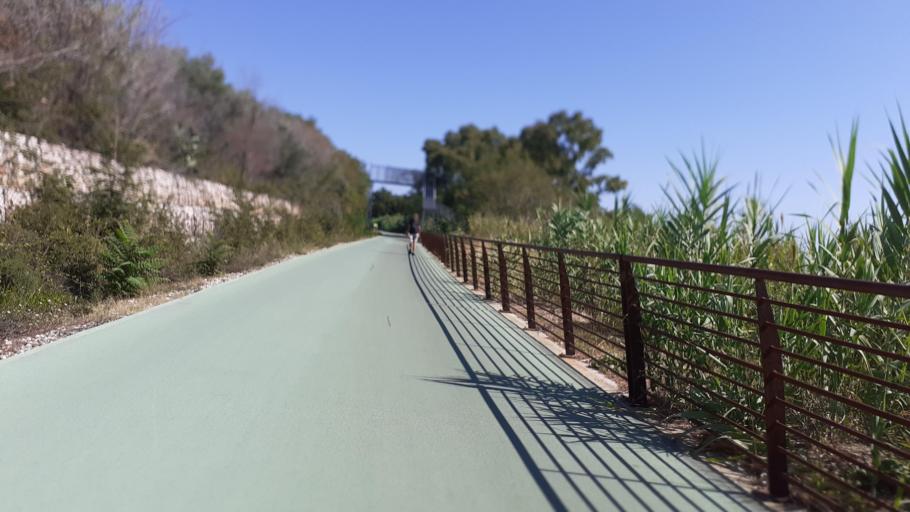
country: IT
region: Abruzzo
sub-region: Provincia di Chieti
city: Vasto
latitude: 42.1113
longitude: 14.7180
